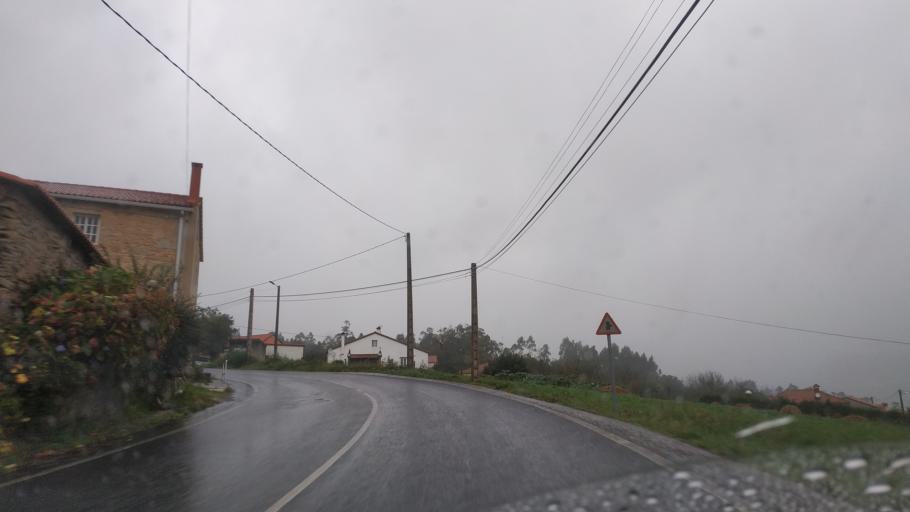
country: ES
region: Galicia
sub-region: Provincia da Coruna
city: Negreira
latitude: 42.9110
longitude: -8.7644
